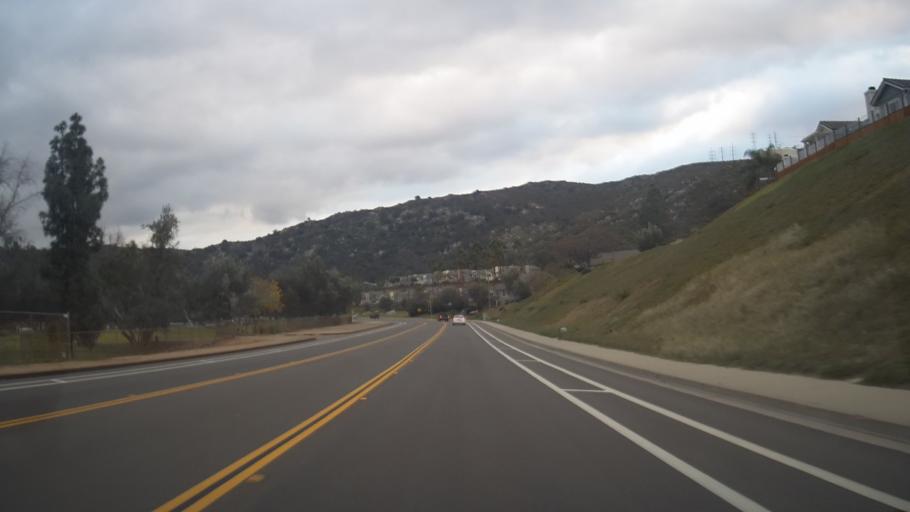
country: US
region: California
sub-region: San Diego County
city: Granite Hills
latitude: 32.7788
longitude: -116.8885
